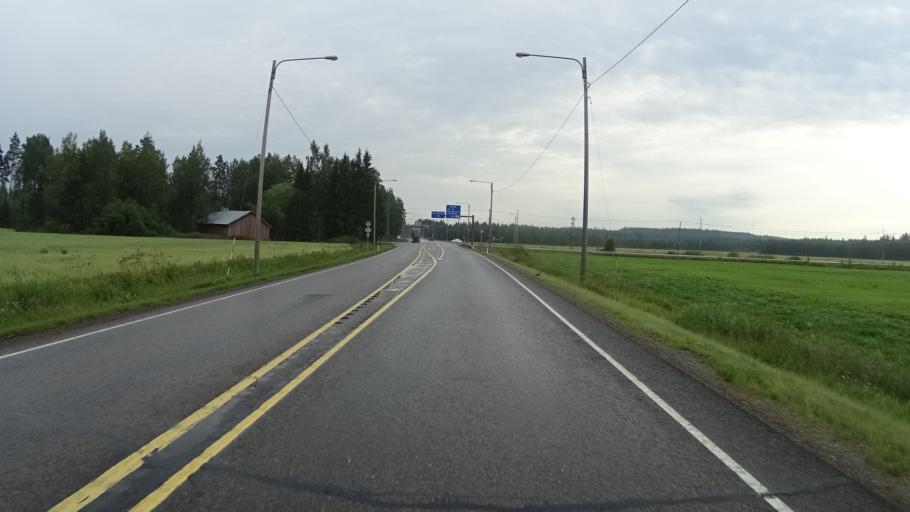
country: FI
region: Kymenlaakso
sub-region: Kouvola
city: Kouvola
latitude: 60.8226
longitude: 26.7874
